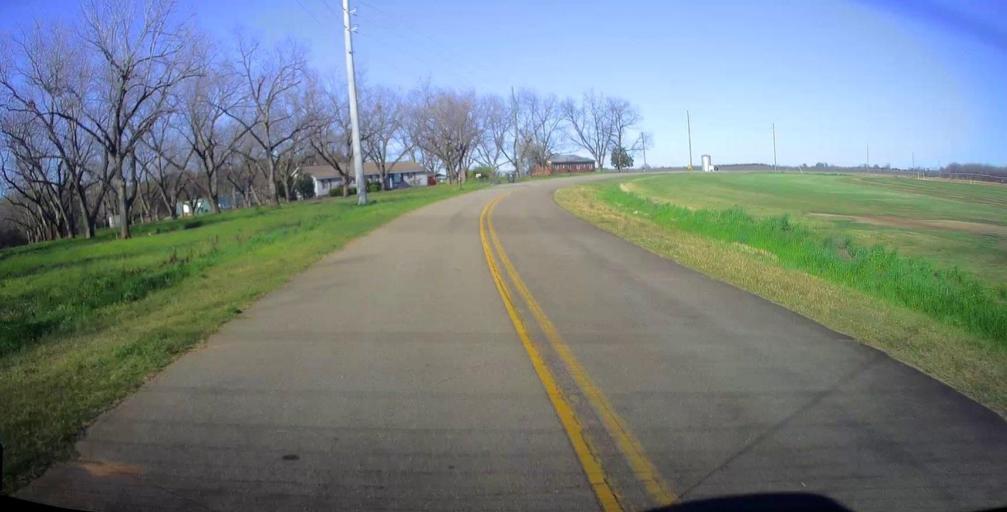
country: US
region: Georgia
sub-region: Macon County
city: Marshallville
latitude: 32.5093
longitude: -83.9461
